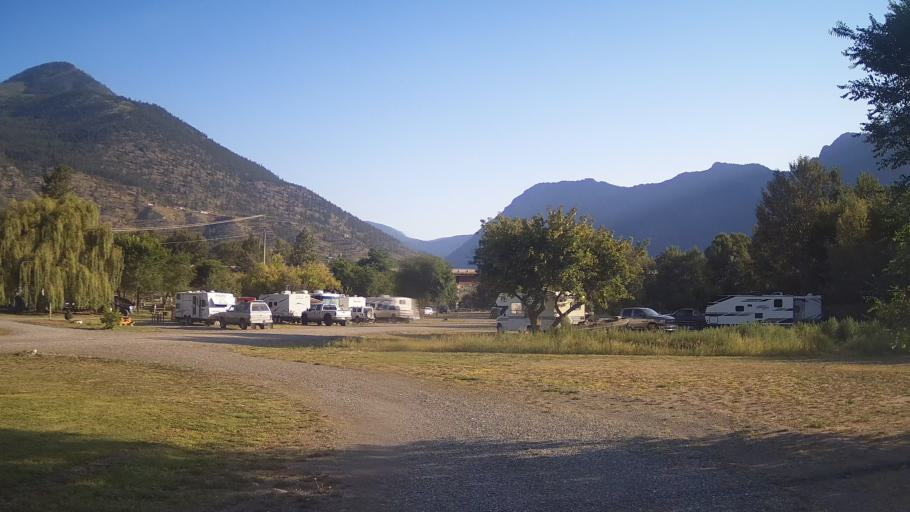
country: CA
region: British Columbia
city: Lillooet
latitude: 50.6808
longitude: -121.9312
